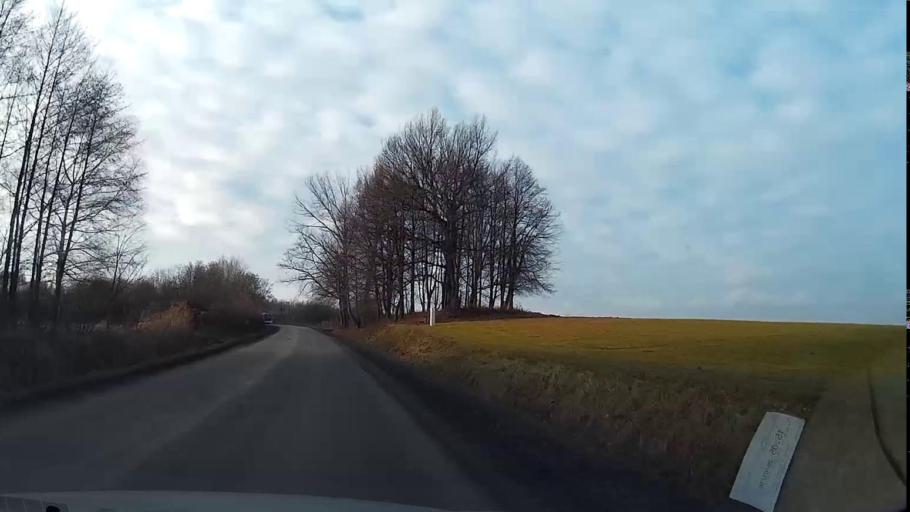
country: PL
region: Lesser Poland Voivodeship
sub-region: Powiat krakowski
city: Czulow
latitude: 50.0637
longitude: 19.6844
